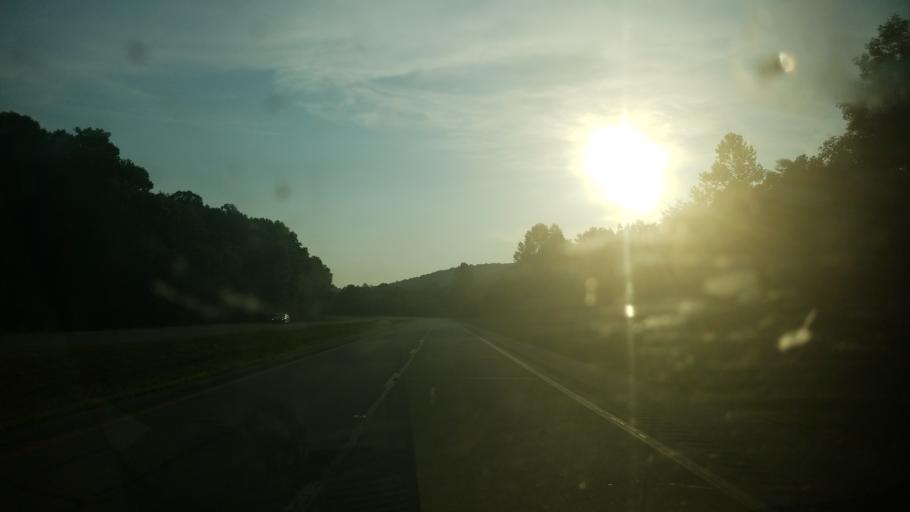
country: US
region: Ohio
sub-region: Adams County
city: Peebles
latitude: 39.0376
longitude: -83.2517
